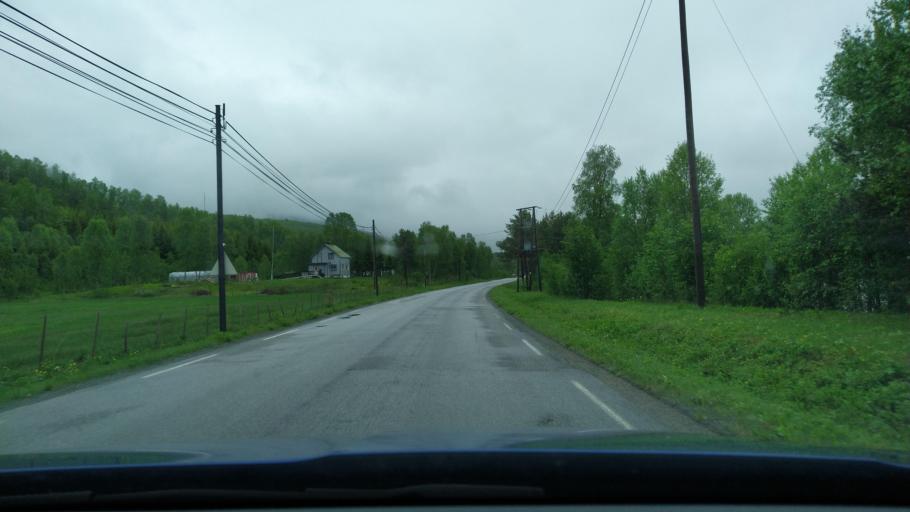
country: NO
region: Troms
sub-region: Dyroy
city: Brostadbotn
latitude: 69.0695
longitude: 17.7347
